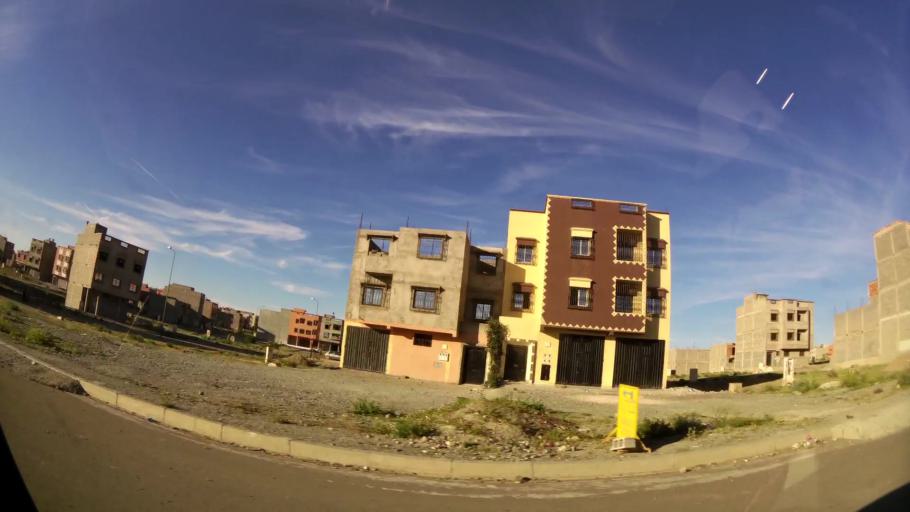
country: MA
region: Marrakech-Tensift-Al Haouz
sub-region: Marrakech
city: Marrakesh
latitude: 31.7672
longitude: -8.0989
